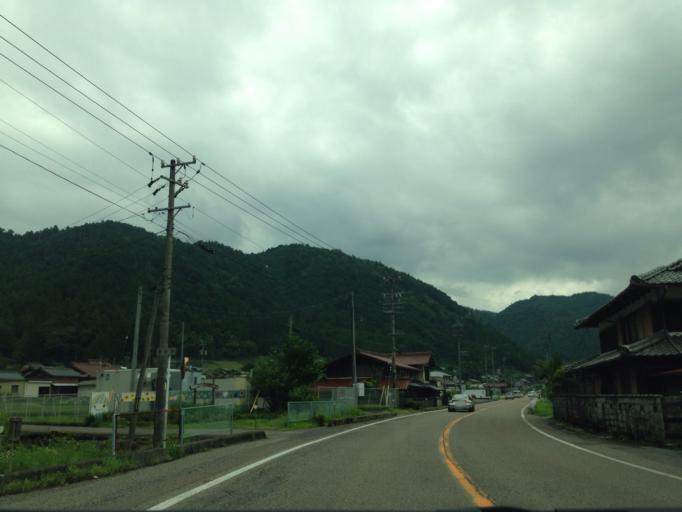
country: JP
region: Gifu
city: Minokamo
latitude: 35.6248
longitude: 137.1681
